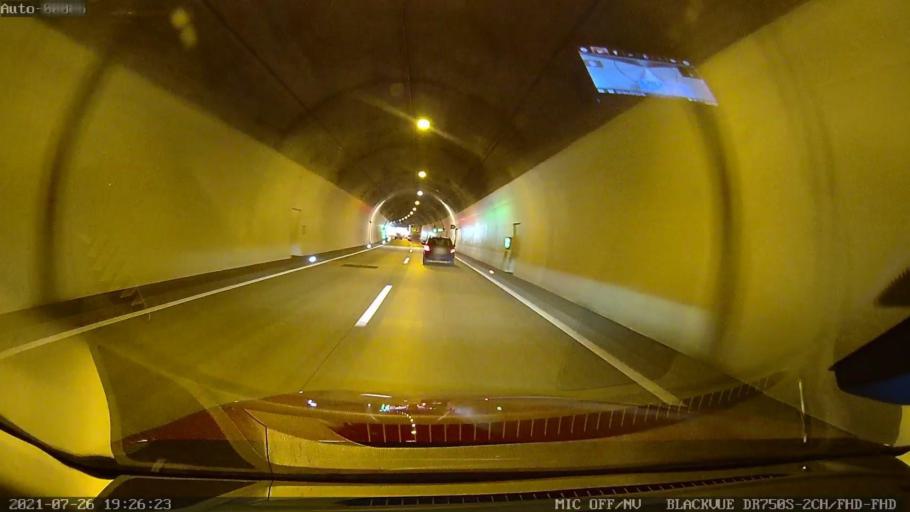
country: AT
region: Upper Austria
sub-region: Politischer Bezirk Kirchdorf an der Krems
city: Micheldorf in Oberoesterreich
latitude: 47.8533
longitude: 14.1597
